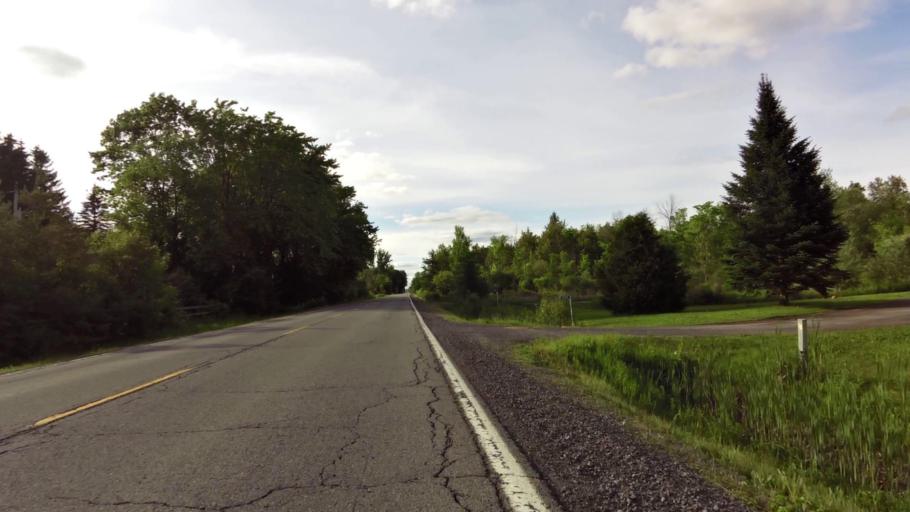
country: CA
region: Ontario
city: Ottawa
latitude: 45.2098
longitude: -75.5968
